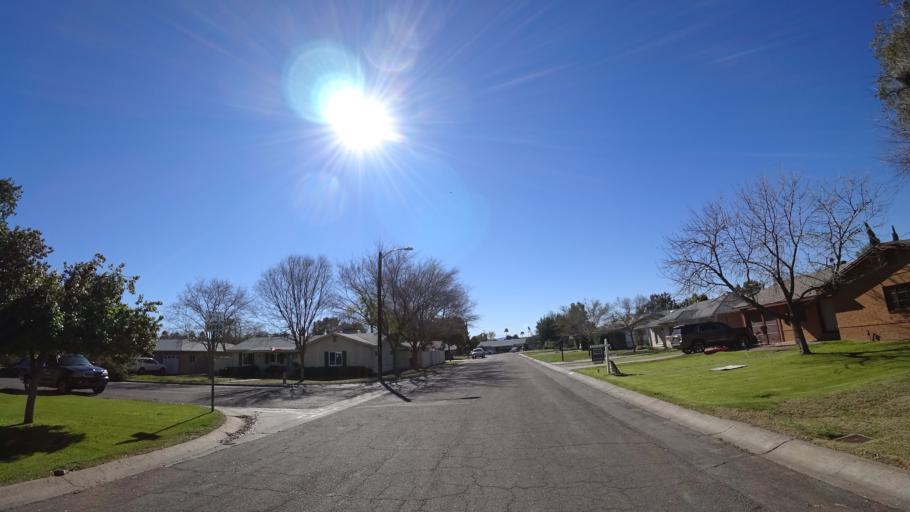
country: US
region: Arizona
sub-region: Maricopa County
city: Phoenix
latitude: 33.5144
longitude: -112.0618
